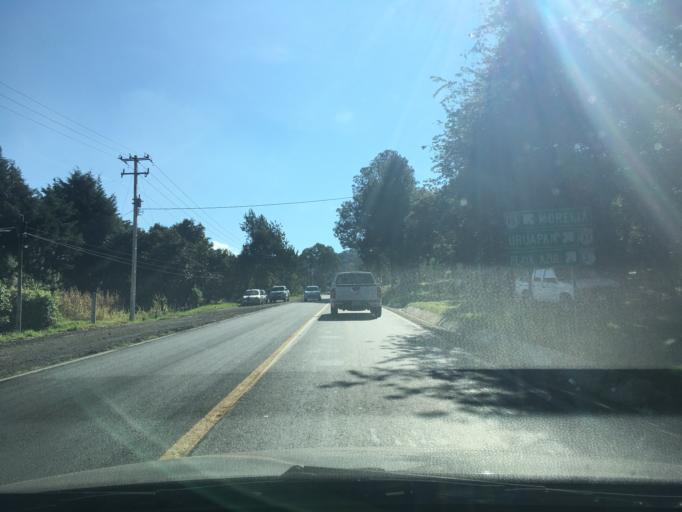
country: MX
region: Michoacan
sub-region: Chilchota
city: Tacuro (Santa Maria Tacuro)
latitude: 19.8527
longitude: -102.0371
